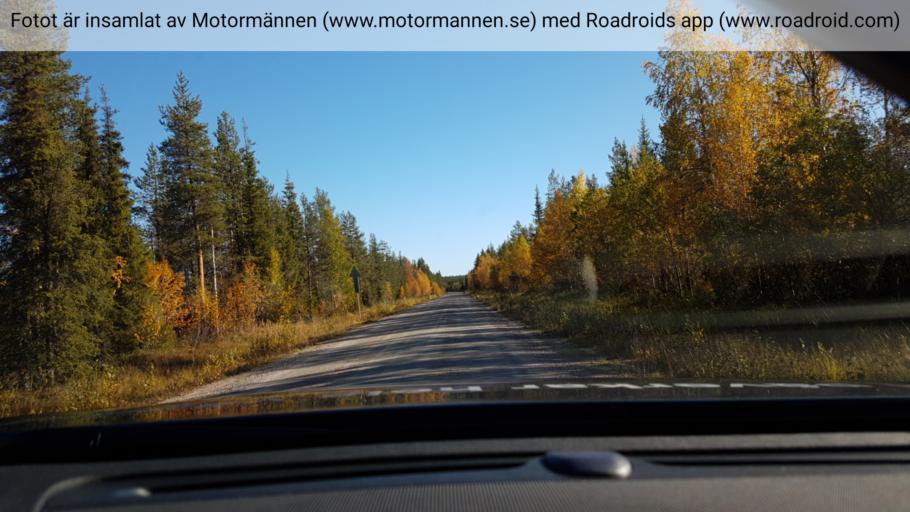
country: SE
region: Norrbotten
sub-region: Gallivare Kommun
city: Gaellivare
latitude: 66.5709
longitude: 21.0234
